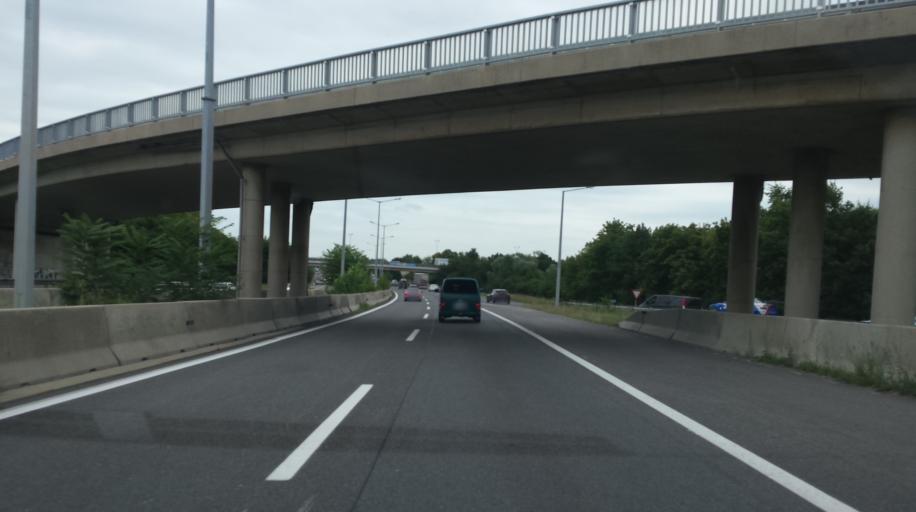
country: AT
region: Lower Austria
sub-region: Politischer Bezirk Modling
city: Brunn am Gebirge
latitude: 48.1169
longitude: 16.2948
